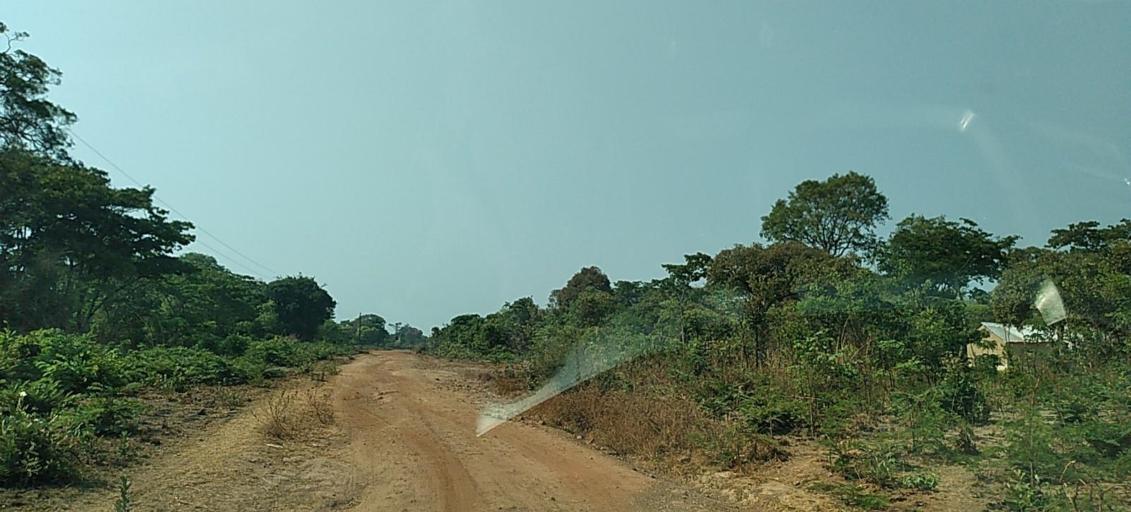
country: ZM
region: Copperbelt
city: Chingola
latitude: -12.9135
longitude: 27.3727
